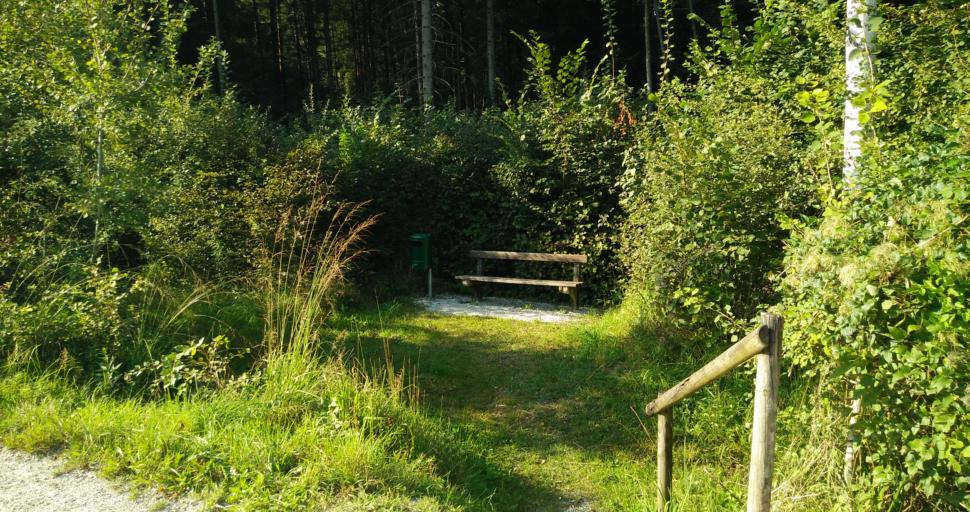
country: AT
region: Salzburg
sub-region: Politischer Bezirk Salzburg-Umgebung
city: Elsbethen
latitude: 47.7309
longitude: 13.0792
